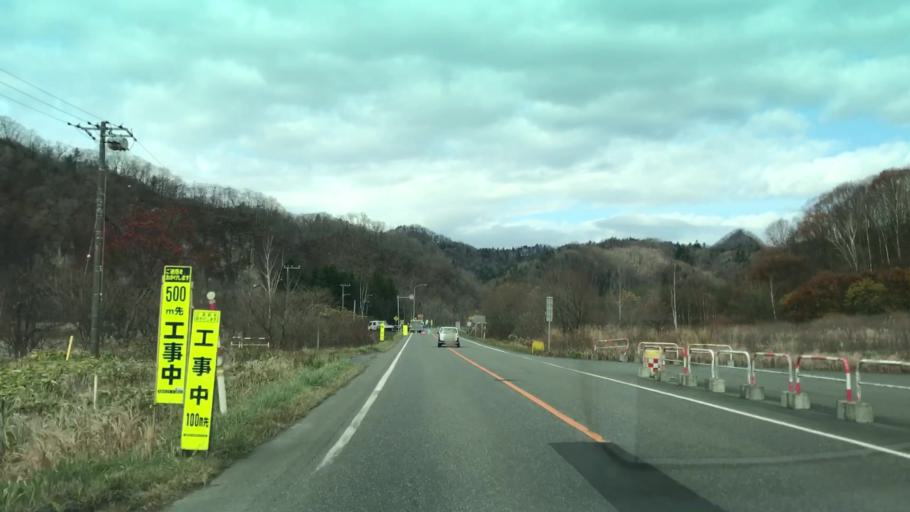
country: JP
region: Hokkaido
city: Shizunai-furukawacho
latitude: 42.7915
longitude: 142.3941
